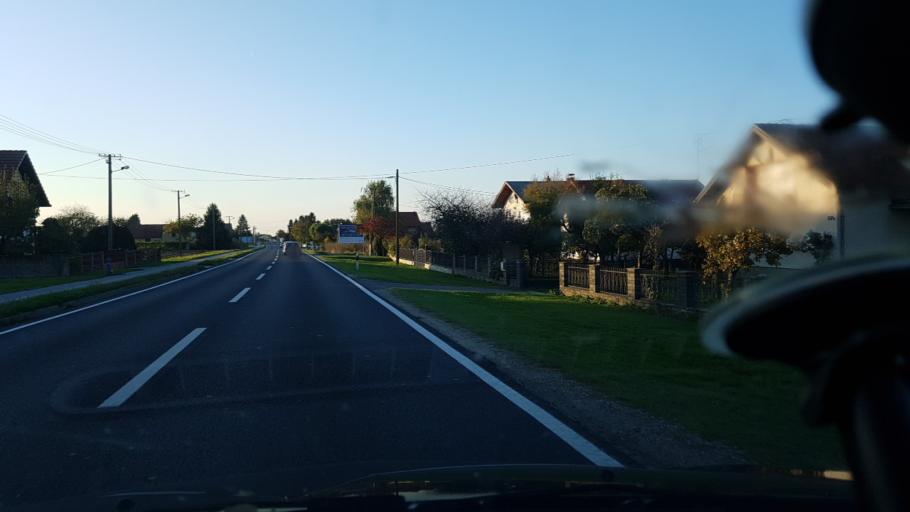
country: HR
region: Koprivnicko-Krizevacka
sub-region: Grad Koprivnica
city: Koprivnica
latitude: 46.1219
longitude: 16.8770
